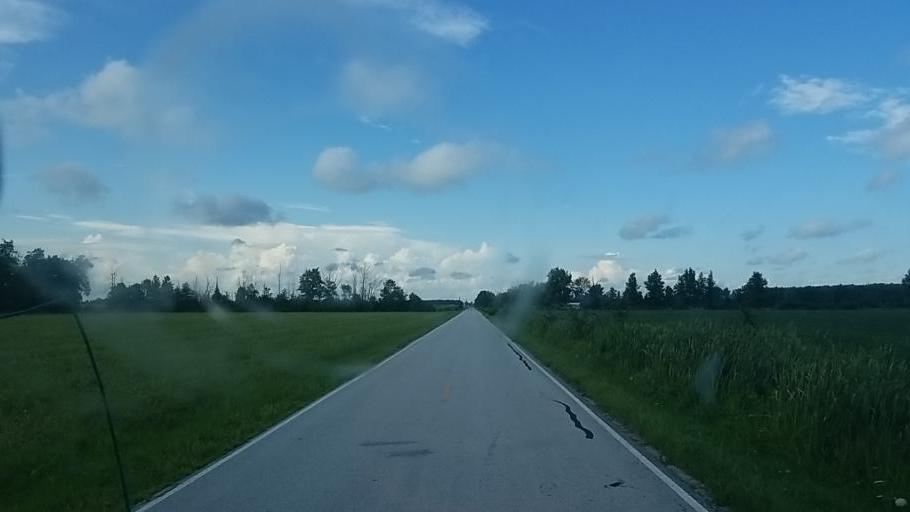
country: US
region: Ohio
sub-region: Hardin County
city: Forest
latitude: 40.7501
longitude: -83.4966
